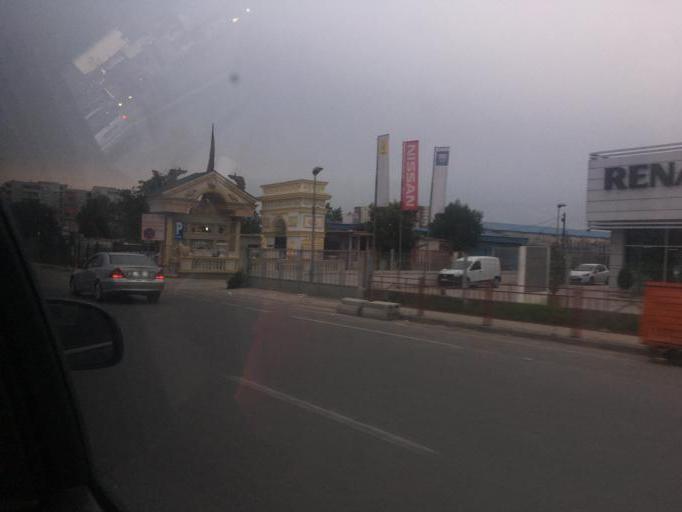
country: AL
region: Tirane
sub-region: Rrethi i Tiranes
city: Paskuqan
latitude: 41.3408
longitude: 19.7822
